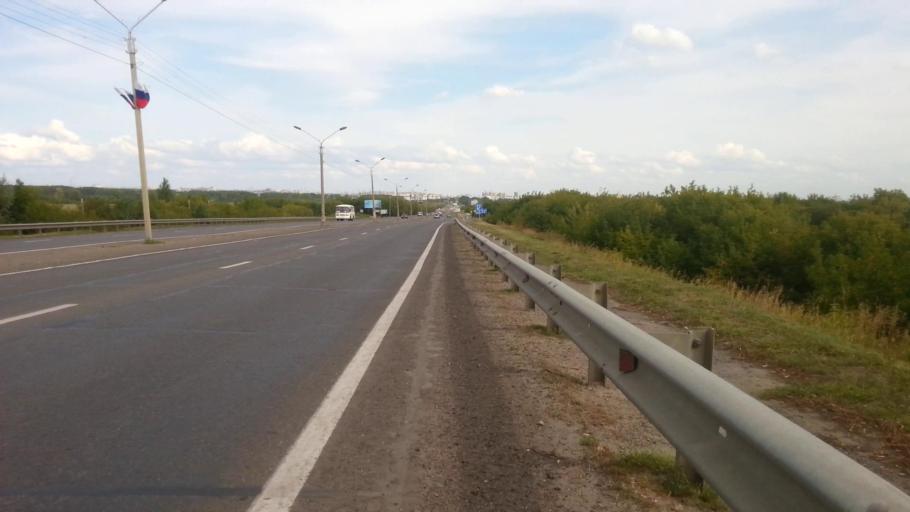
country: RU
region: Altai Krai
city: Novosilikatnyy
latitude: 53.3511
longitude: 83.5908
